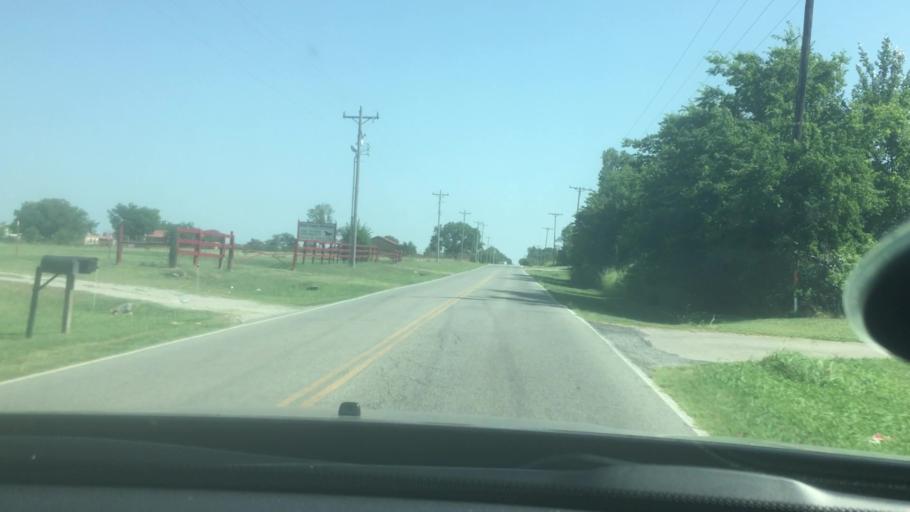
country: US
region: Oklahoma
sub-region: Bryan County
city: Calera
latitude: 34.0044
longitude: -96.4656
